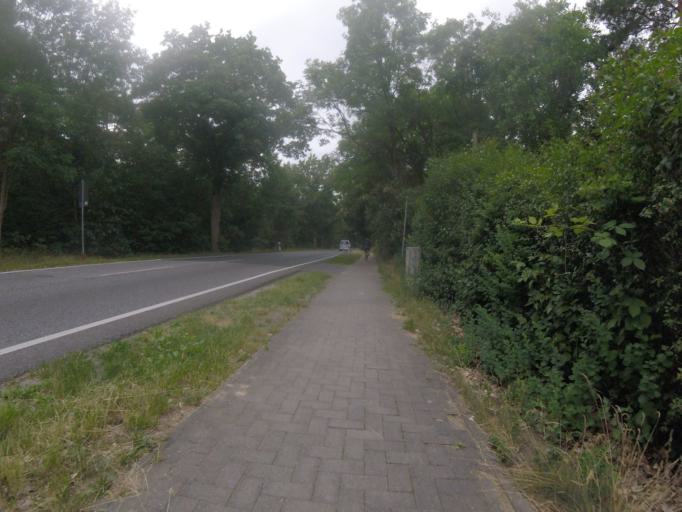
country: DE
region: Brandenburg
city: Bestensee
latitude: 52.2621
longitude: 13.6333
